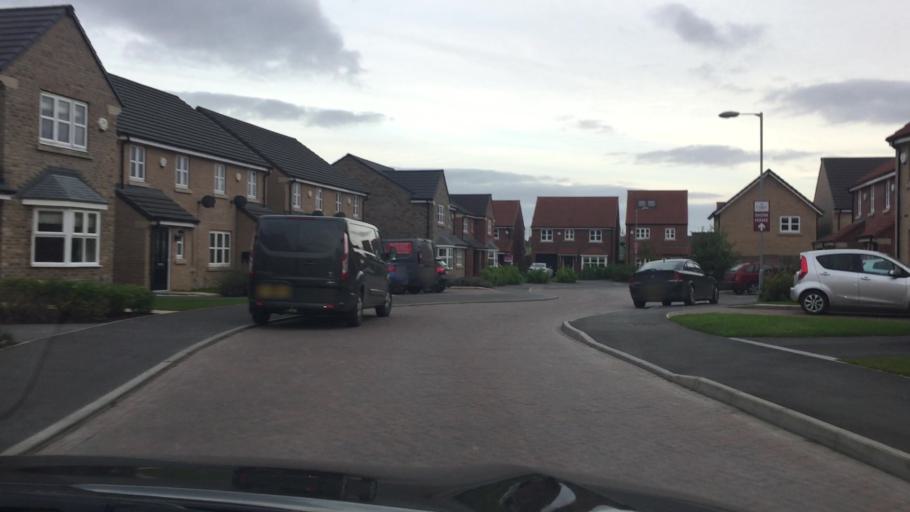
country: GB
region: England
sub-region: East Riding of Yorkshire
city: Pocklington
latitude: 53.9254
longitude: -0.7826
